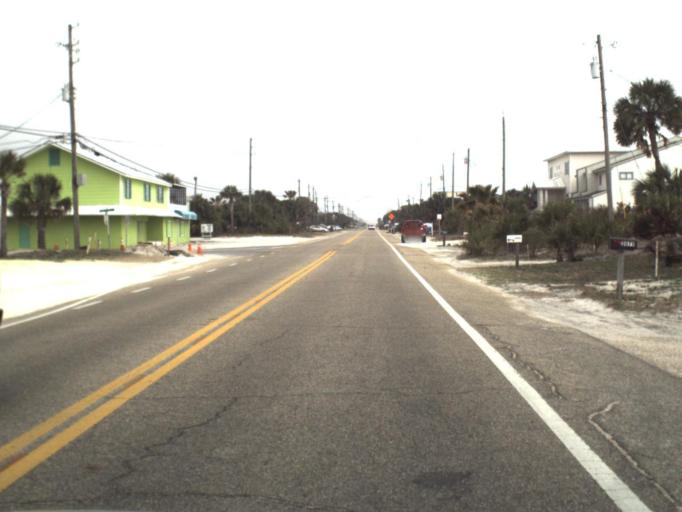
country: US
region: Florida
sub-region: Bay County
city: Laguna Beach
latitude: 30.2471
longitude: -85.9412
